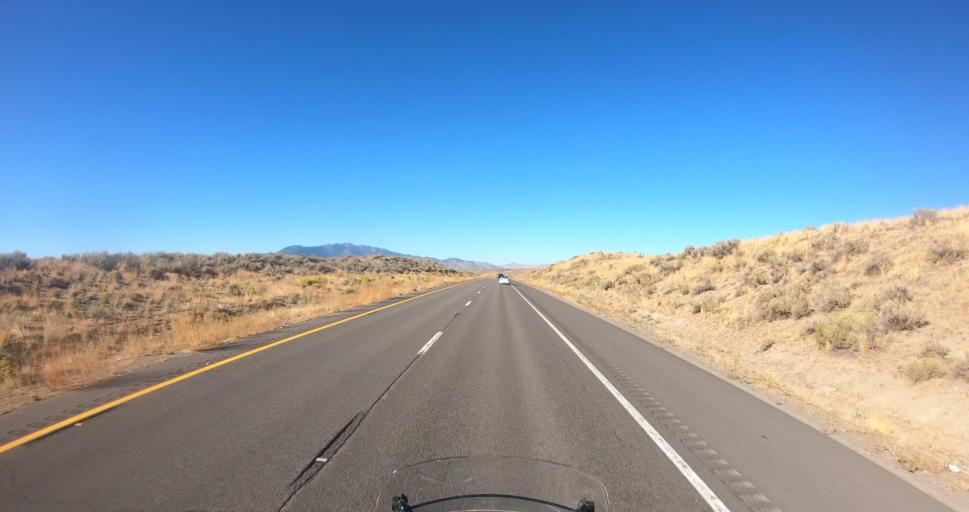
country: US
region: Nevada
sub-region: Washoe County
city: Cold Springs
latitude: 39.7594
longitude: -120.0387
